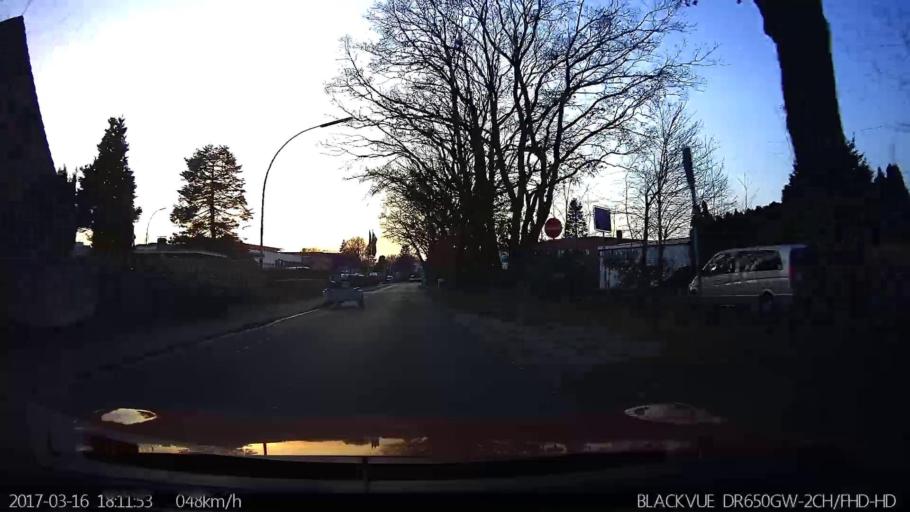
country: DE
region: Schleswig-Holstein
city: Halstenbek
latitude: 53.6321
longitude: 9.8652
